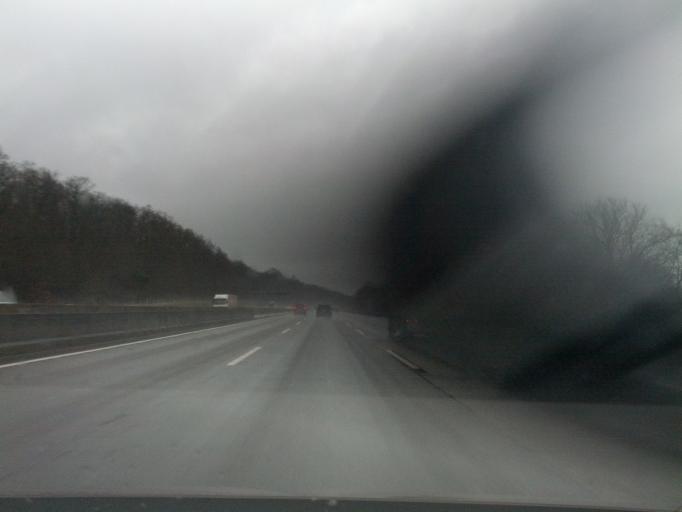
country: DE
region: Hesse
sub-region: Regierungsbezirk Darmstadt
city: Rosbach vor der Hohe
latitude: 50.2952
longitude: 8.6732
